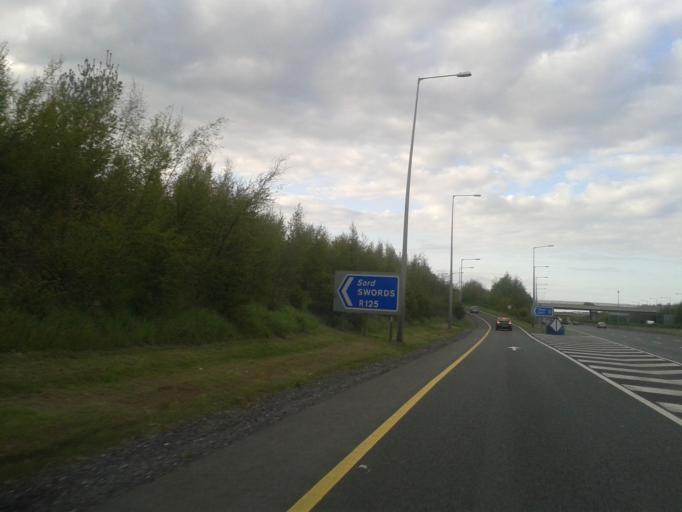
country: IE
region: Leinster
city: Kinsealy-Drinan
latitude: 53.4404
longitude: -6.2076
